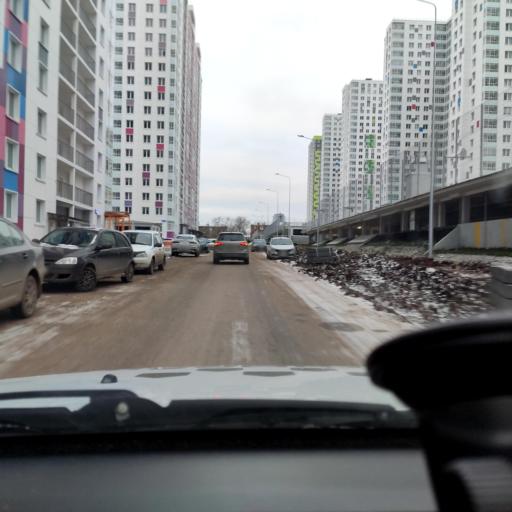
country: RU
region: Perm
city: Perm
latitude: 57.9915
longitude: 56.2661
